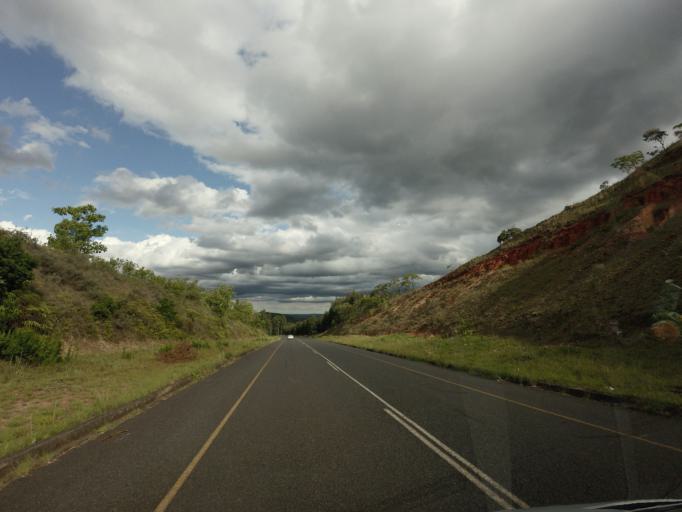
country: ZA
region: Mpumalanga
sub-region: Ehlanzeni District
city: Graksop
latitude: -24.9883
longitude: 30.9818
